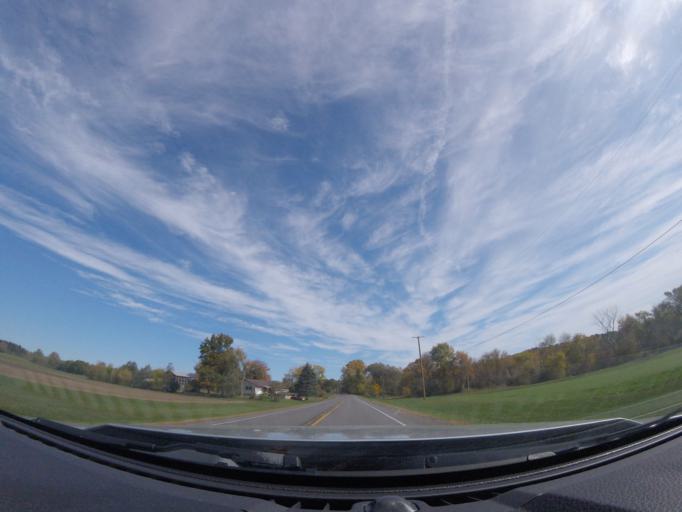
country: US
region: New York
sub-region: Tompkins County
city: Dryden
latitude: 42.5190
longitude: -76.3310
